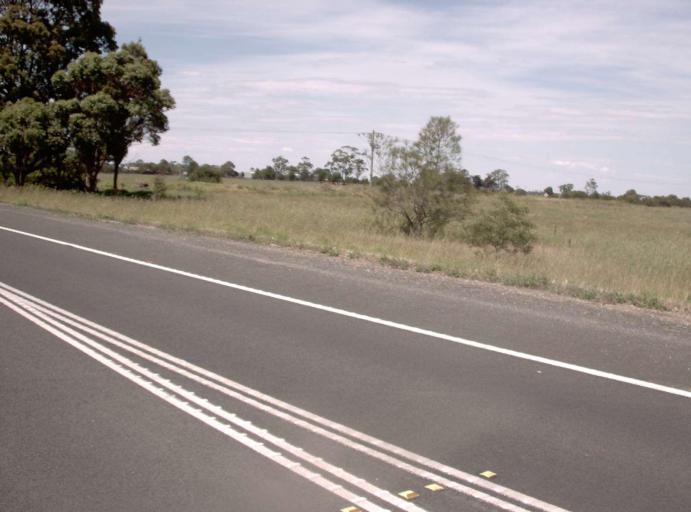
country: AU
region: Victoria
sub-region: Wellington
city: Sale
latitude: -38.0691
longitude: 147.0738
